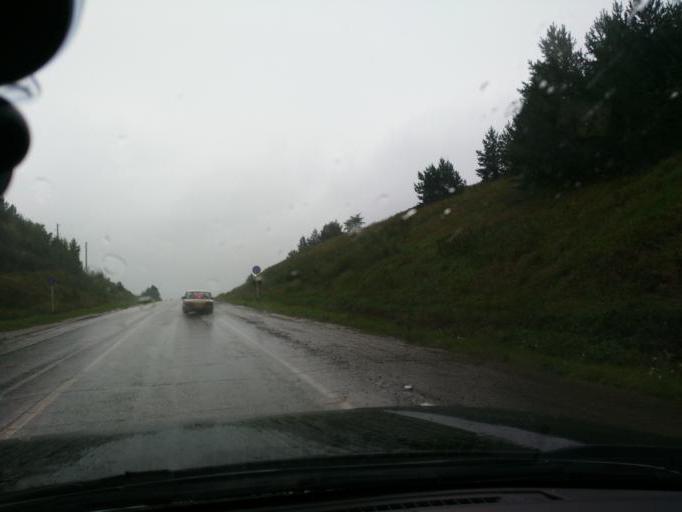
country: RU
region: Perm
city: Osa
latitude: 57.1917
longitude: 55.5913
